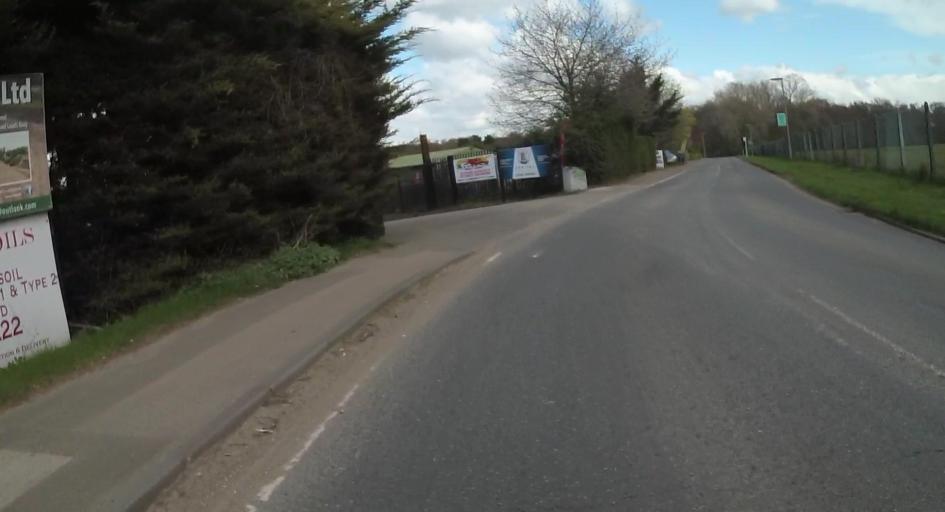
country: GB
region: England
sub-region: Surrey
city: Ottershaw
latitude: 51.3524
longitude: -0.5154
